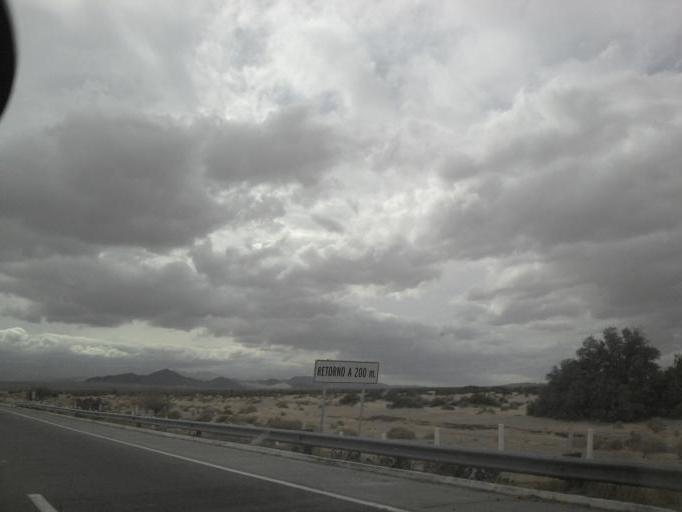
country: MX
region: Baja California
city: Progreso
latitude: 32.5742
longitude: -115.7702
